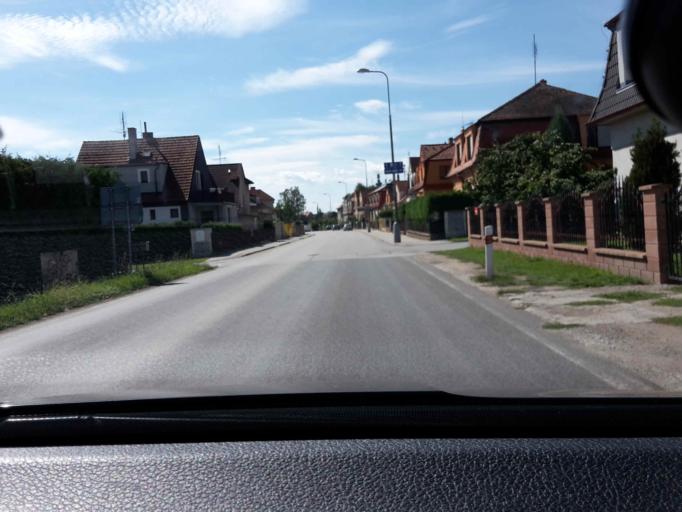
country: CZ
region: Jihocesky
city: Sobeslav
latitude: 49.2643
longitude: 14.7276
